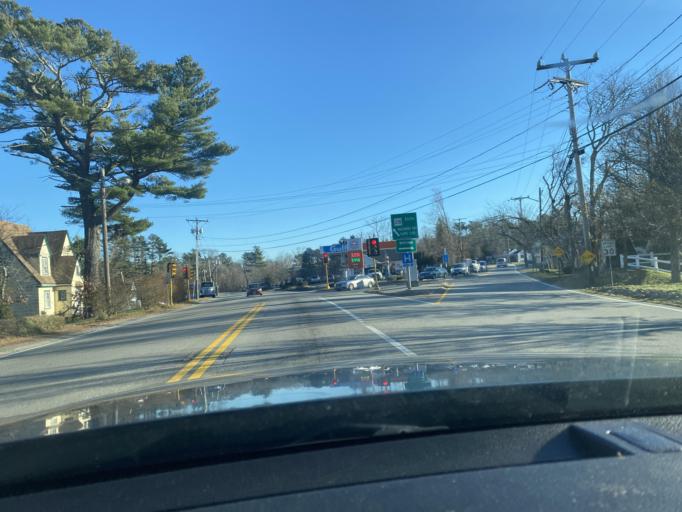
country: US
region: Massachusetts
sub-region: Plymouth County
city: Wareham Center
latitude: 41.7691
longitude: -70.7321
